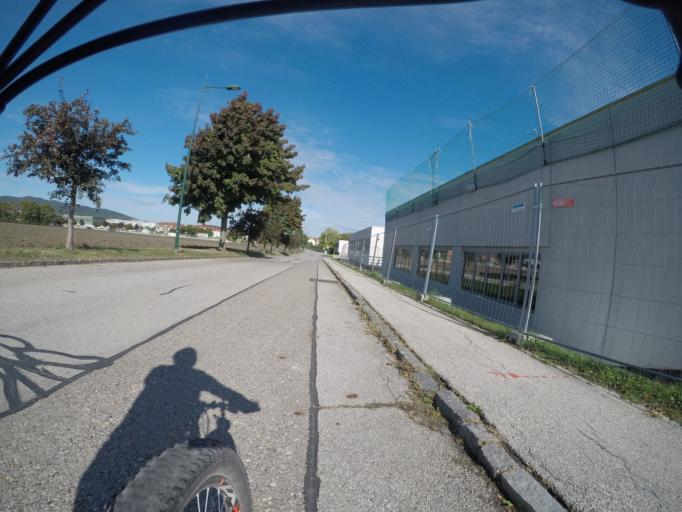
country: AT
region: Lower Austria
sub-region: Politischer Bezirk Modling
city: Modling
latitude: 48.0989
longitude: 16.3014
